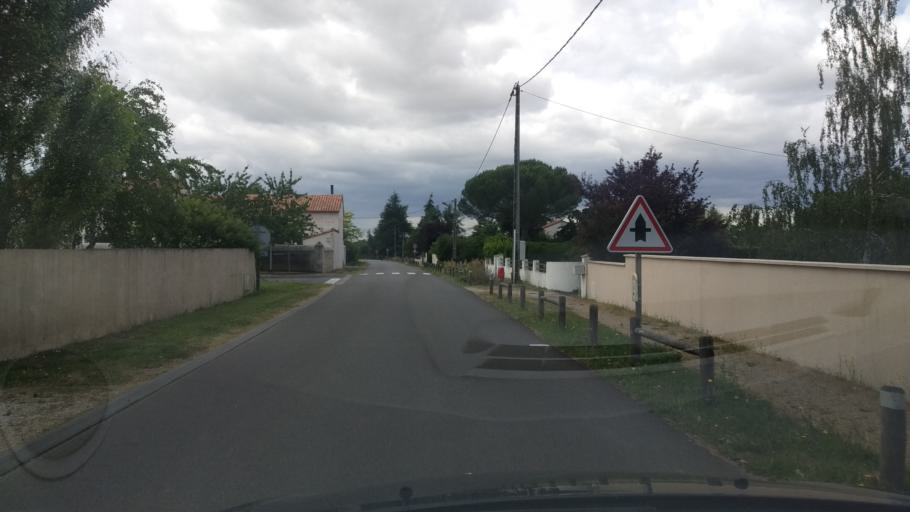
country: FR
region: Poitou-Charentes
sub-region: Departement de la Vienne
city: Cisse
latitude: 46.6220
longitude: 0.2041
